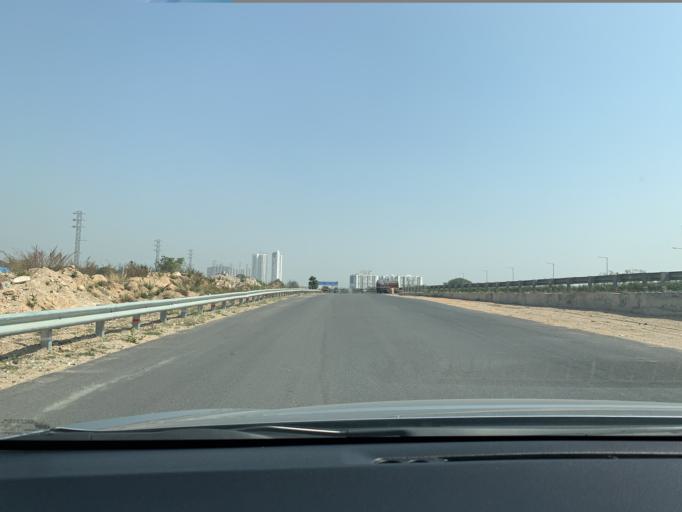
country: IN
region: Telangana
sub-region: Medak
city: Serilingampalle
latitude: 17.4061
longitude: 78.3332
